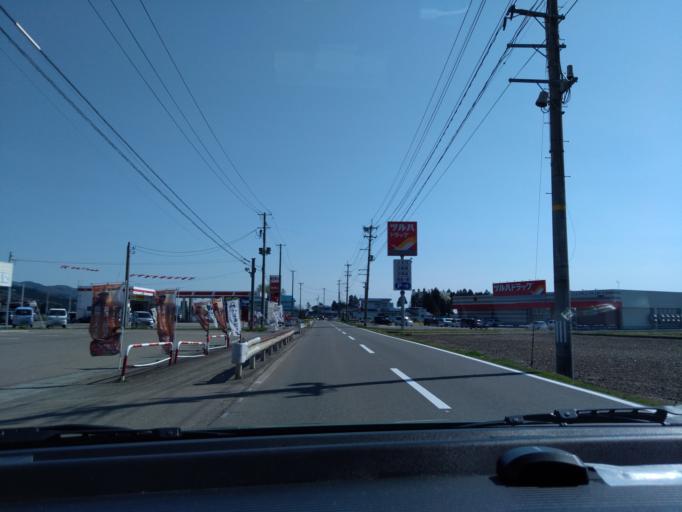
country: JP
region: Akita
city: Omagari
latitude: 39.4603
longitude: 140.5801
